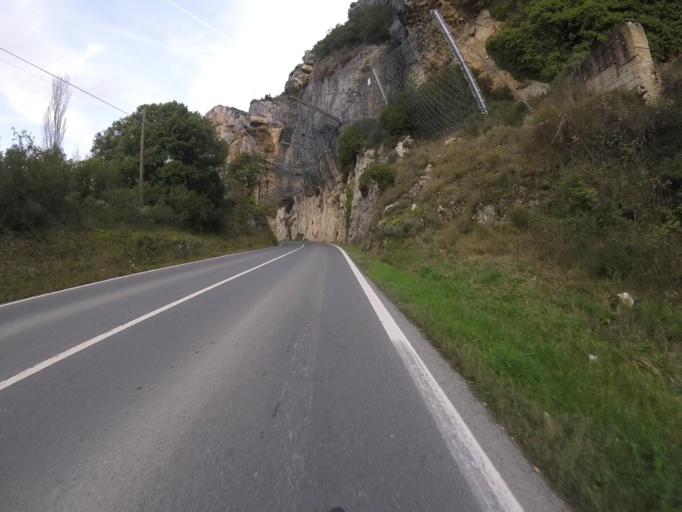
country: ES
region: Navarre
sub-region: Provincia de Navarra
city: Estella
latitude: 42.6995
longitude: -2.0564
